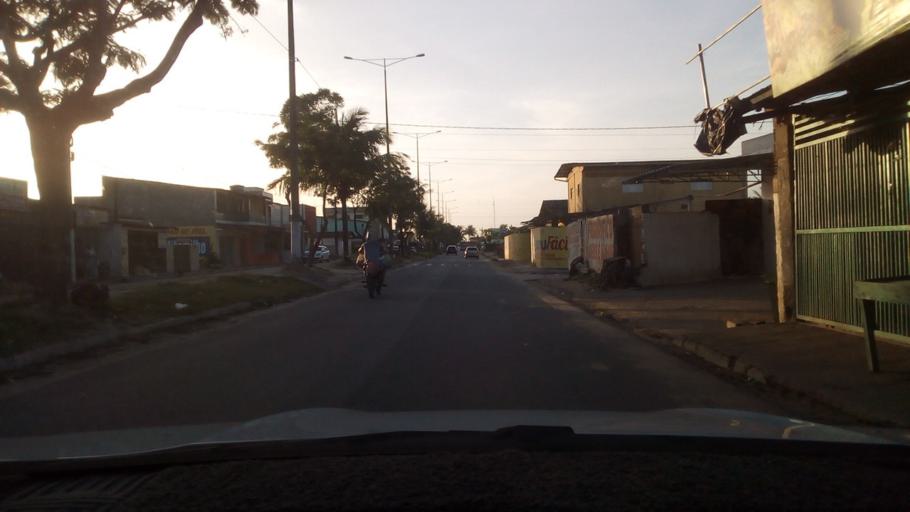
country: BR
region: Paraiba
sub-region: Bayeux
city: Bayeux
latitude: -7.1751
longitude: -34.9277
